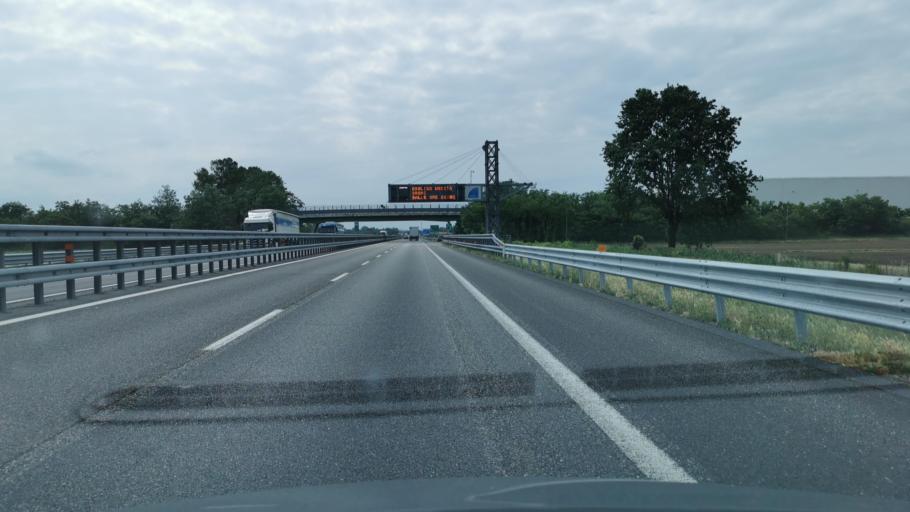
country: IT
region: Emilia-Romagna
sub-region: Provincia di Piacenza
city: Castel San Giovanni
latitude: 45.0739
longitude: 9.4655
